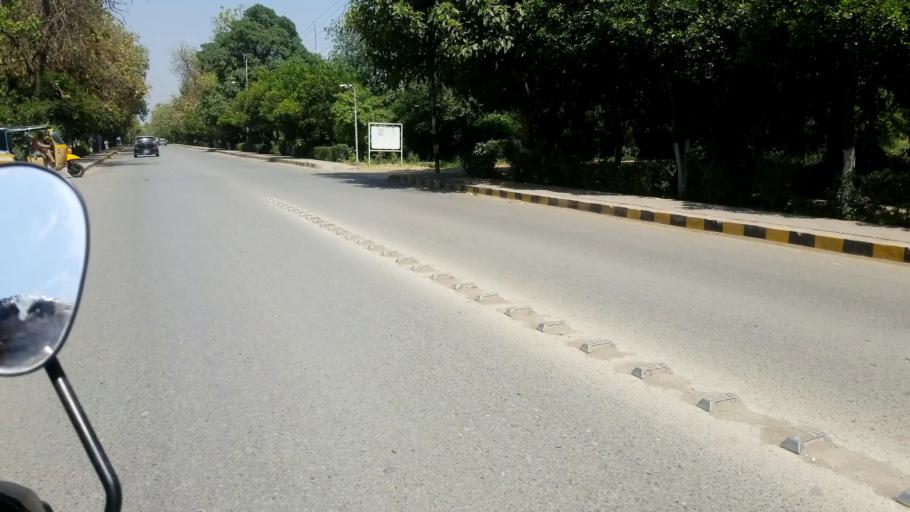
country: PK
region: Khyber Pakhtunkhwa
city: Peshawar
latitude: 34.0002
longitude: 71.4862
